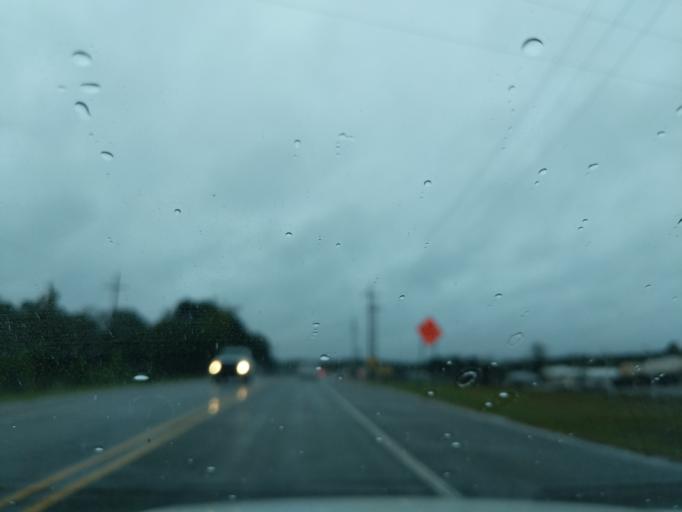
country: US
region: Louisiana
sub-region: Webster Parish
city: Minden
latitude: 32.6048
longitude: -93.2498
